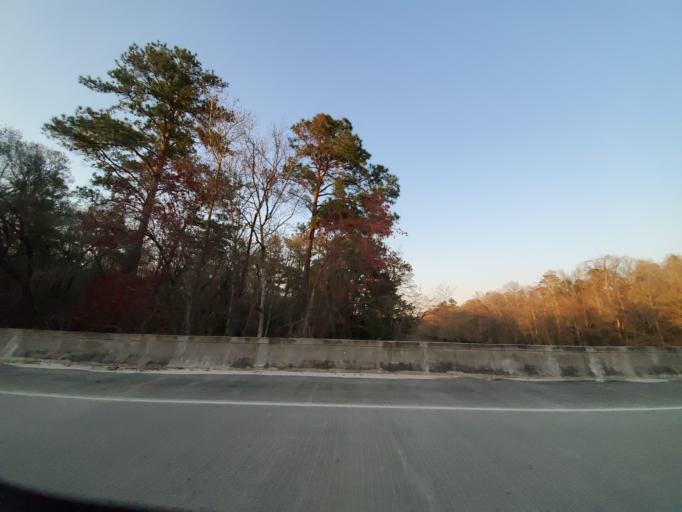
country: US
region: South Carolina
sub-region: Dorchester County
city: Ridgeville
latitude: 33.0277
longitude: -80.3930
